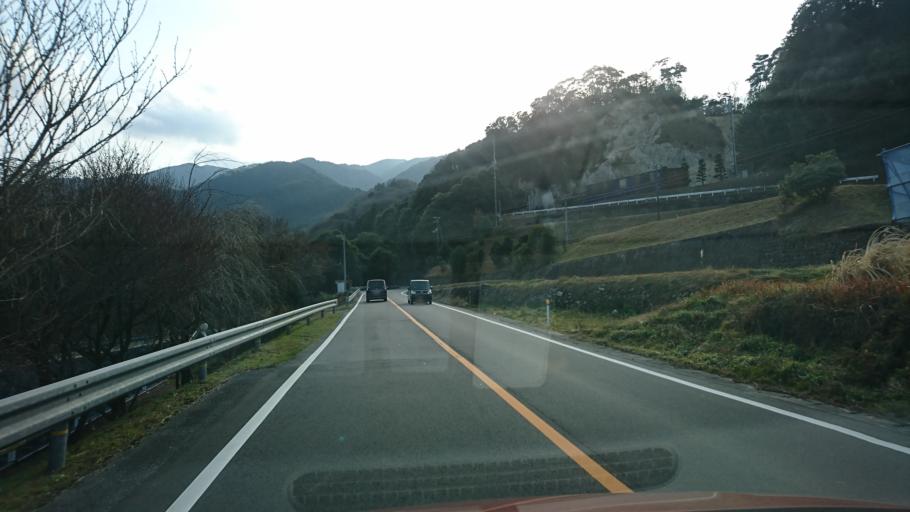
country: JP
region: Ehime
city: Hojo
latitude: 33.9748
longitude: 132.9034
